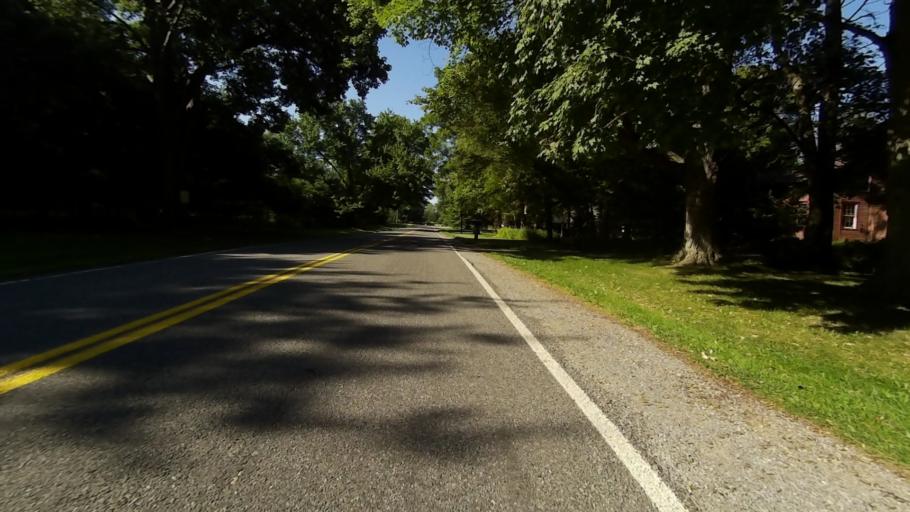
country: US
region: Ohio
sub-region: Portage County
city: Kent
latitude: 41.1902
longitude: -81.3340
